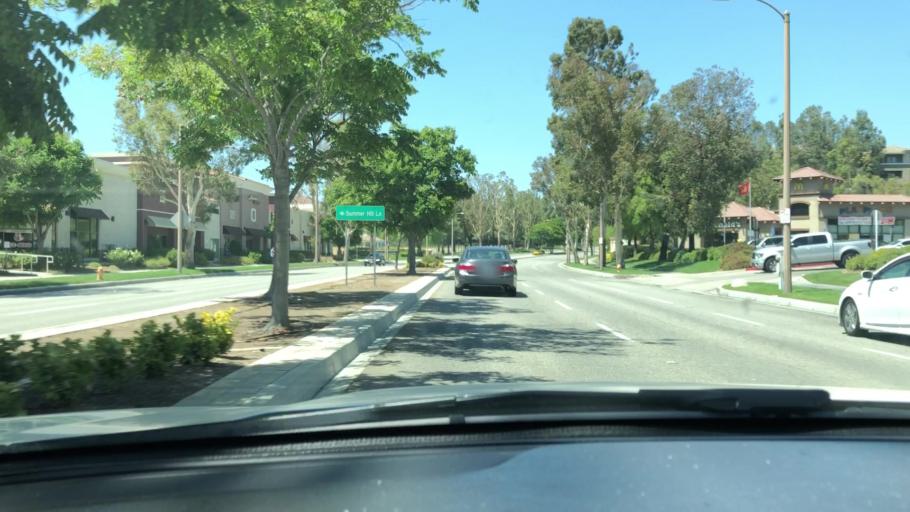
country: US
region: California
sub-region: Los Angeles County
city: Santa Clarita
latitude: 34.4453
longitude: -118.5533
